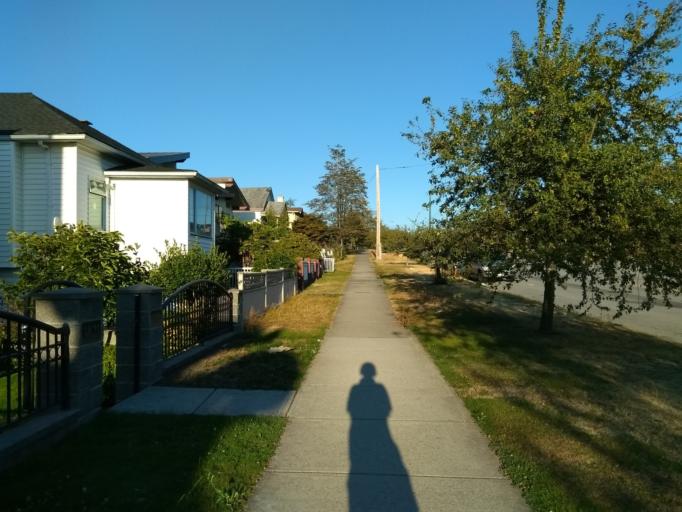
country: CA
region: British Columbia
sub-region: Fraser Valley Regional District
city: North Vancouver
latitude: 49.2447
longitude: -123.0411
